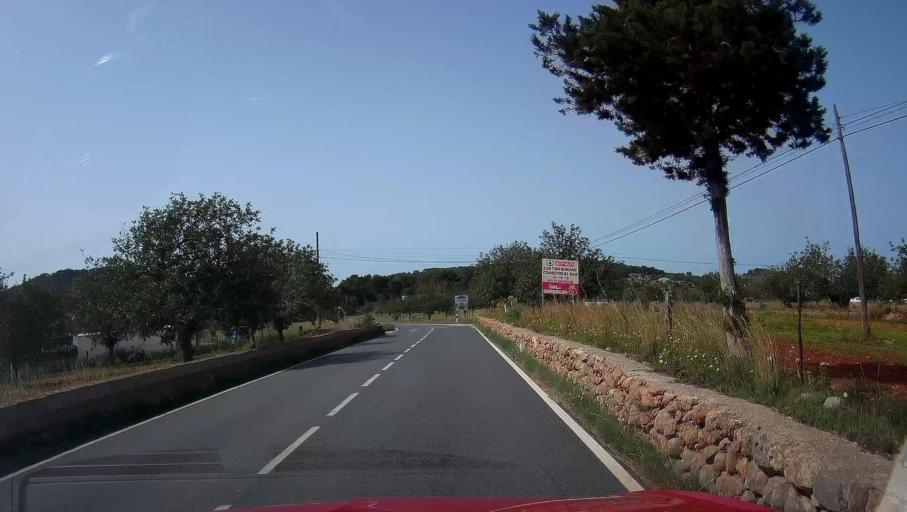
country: ES
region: Balearic Islands
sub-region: Illes Balears
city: Sant Joan de Labritja
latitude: 39.0502
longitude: 1.5723
